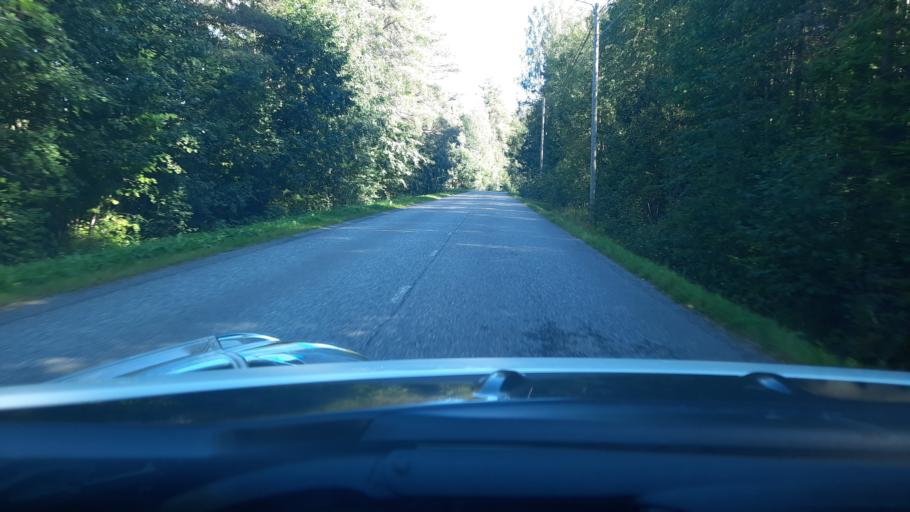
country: FI
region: North Karelia
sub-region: Joensuu
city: Joensuu
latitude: 62.6358
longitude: 29.6972
